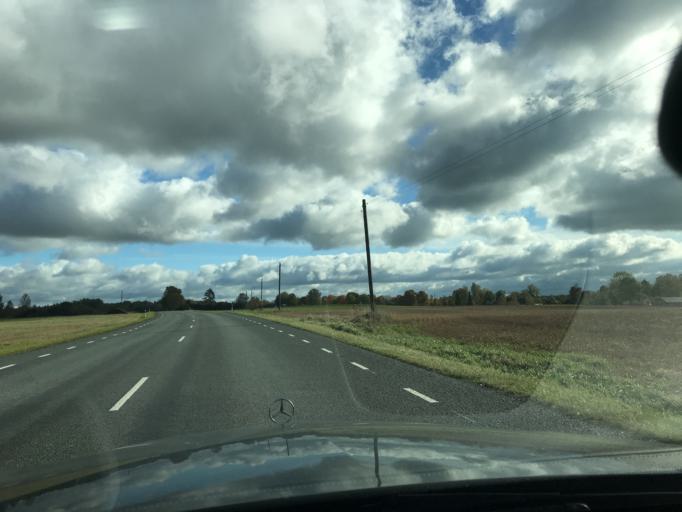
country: EE
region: Vorumaa
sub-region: Antsla vald
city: Vana-Antsla
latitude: 57.9120
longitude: 26.3980
